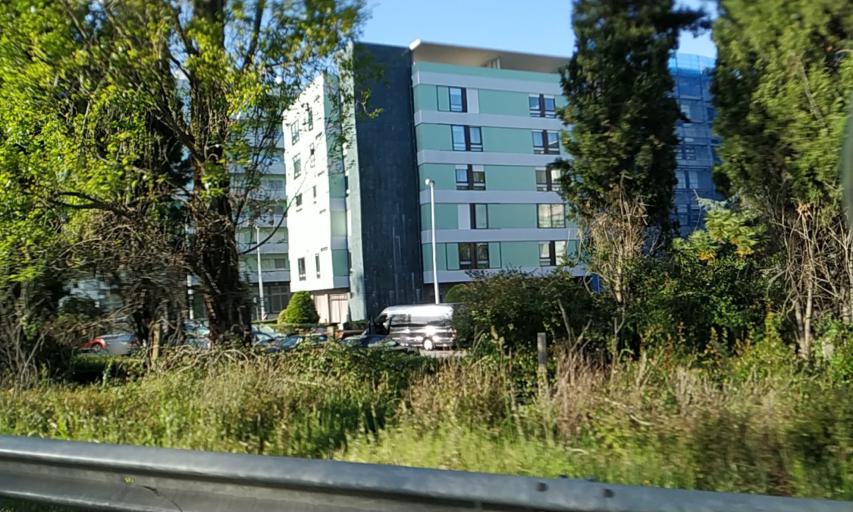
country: PT
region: Porto
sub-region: Maia
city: Pedroucos
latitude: 41.1804
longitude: -8.5915
